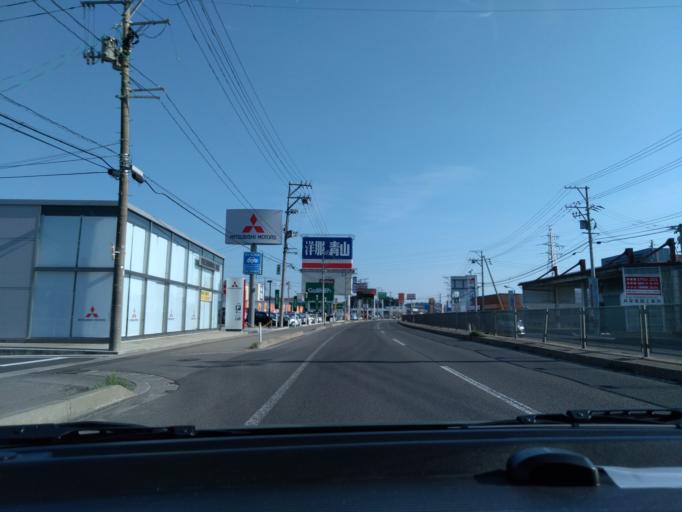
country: JP
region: Akita
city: Yokotemachi
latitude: 39.3072
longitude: 140.5577
